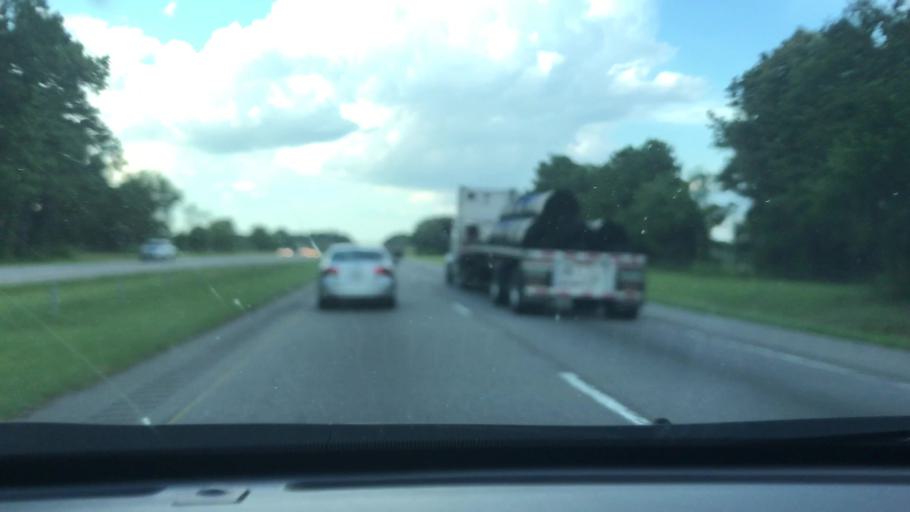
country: US
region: North Carolina
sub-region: Robeson County
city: Saint Pauls
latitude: 34.8756
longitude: -78.9626
